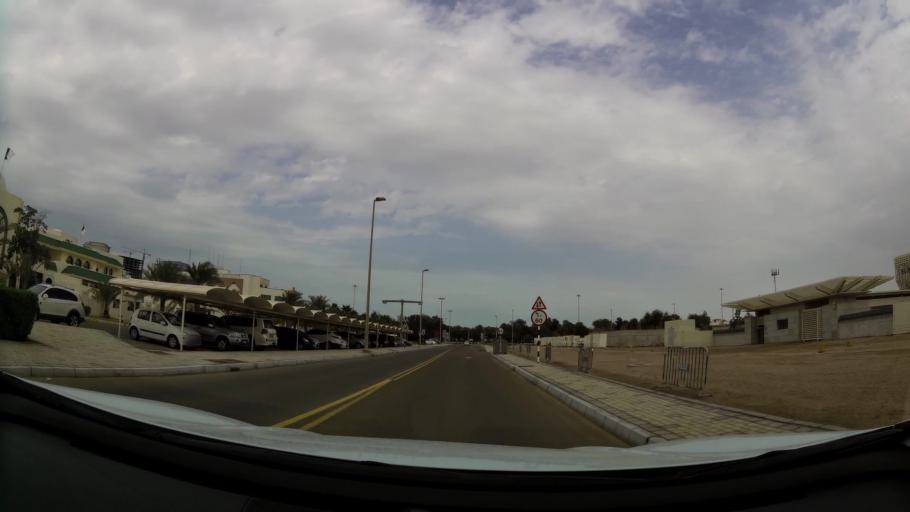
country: AE
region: Abu Dhabi
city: Abu Dhabi
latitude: 24.4246
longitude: 54.4409
